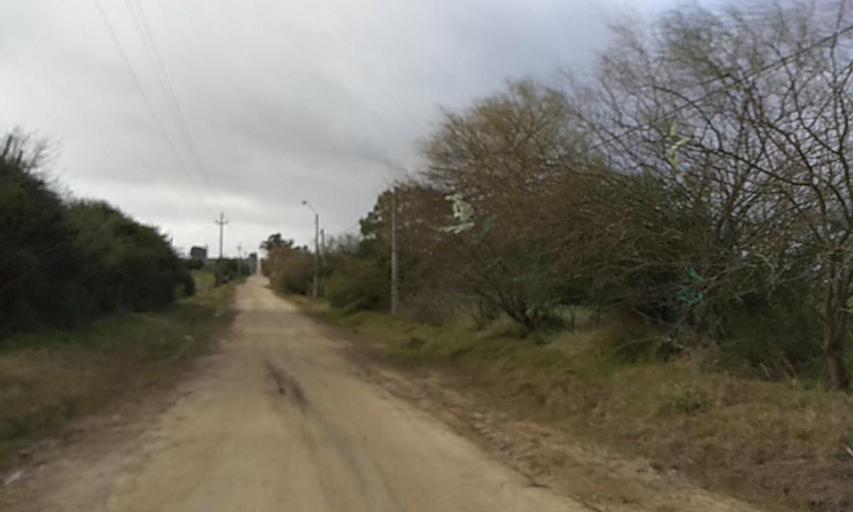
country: UY
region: Florida
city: Florida
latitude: -34.0576
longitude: -56.2225
